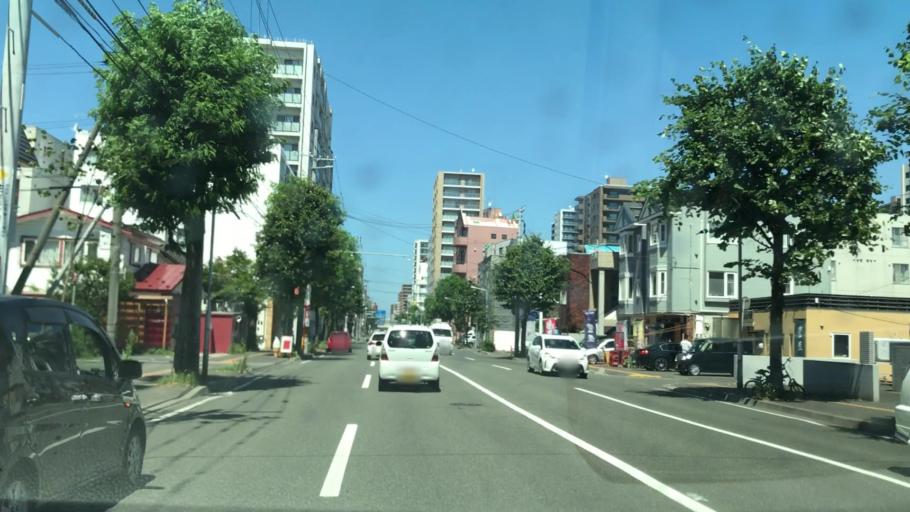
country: JP
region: Hokkaido
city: Sapporo
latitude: 43.0531
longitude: 141.3210
